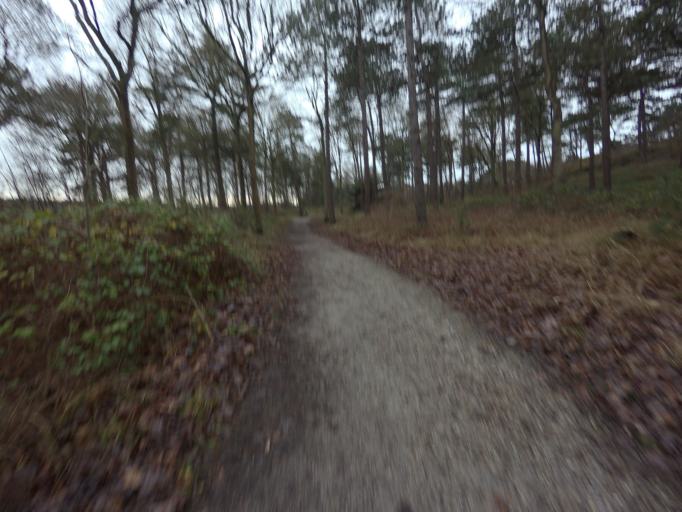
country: NL
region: North Holland
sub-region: Gemeente Texel
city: Den Burg
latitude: 53.0847
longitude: 4.7513
